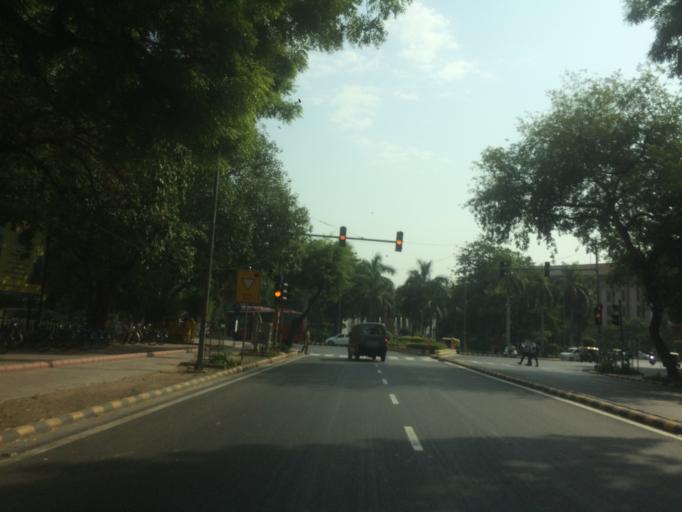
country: IN
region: NCT
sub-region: New Delhi
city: New Delhi
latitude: 28.6226
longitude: 77.2121
